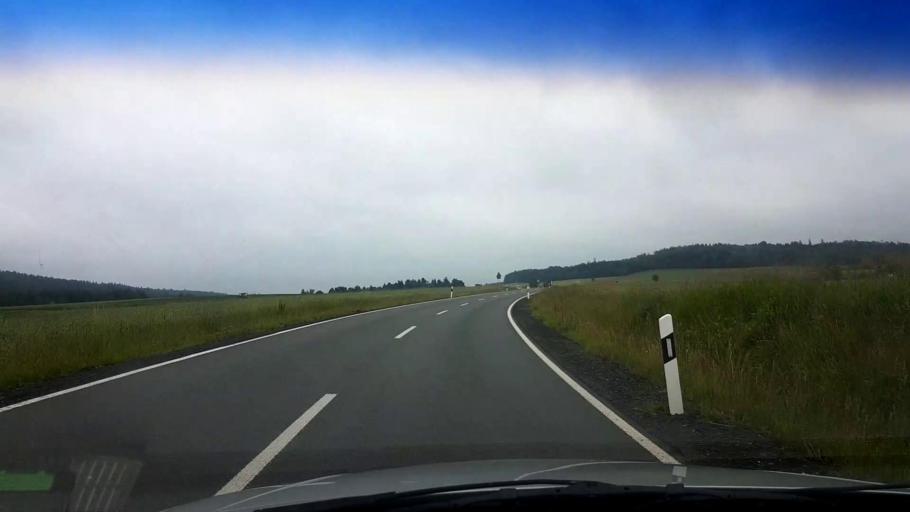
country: DE
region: Bavaria
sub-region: Upper Franconia
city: Arzberg
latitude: 50.0295
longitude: 12.1727
